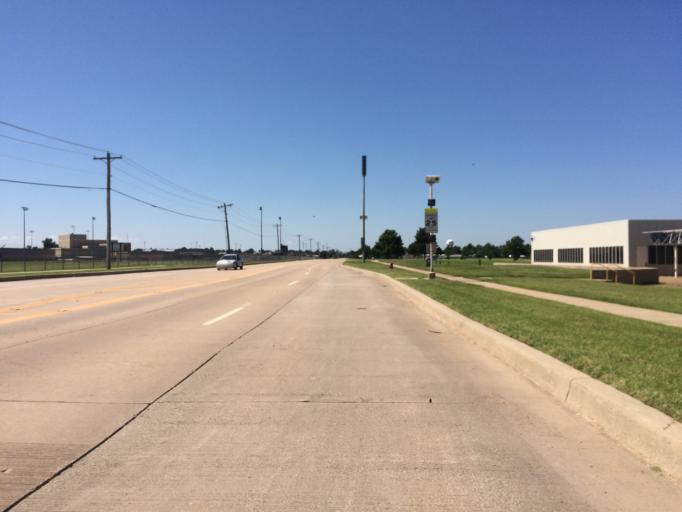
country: US
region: Oklahoma
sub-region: Cleveland County
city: Norman
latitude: 35.2468
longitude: -97.4501
